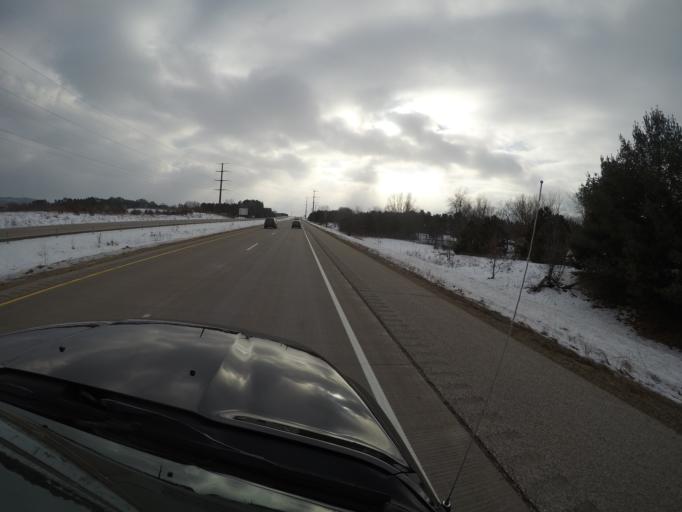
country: US
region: Wisconsin
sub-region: La Crosse County
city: Holmen
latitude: 43.9772
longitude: -91.2863
